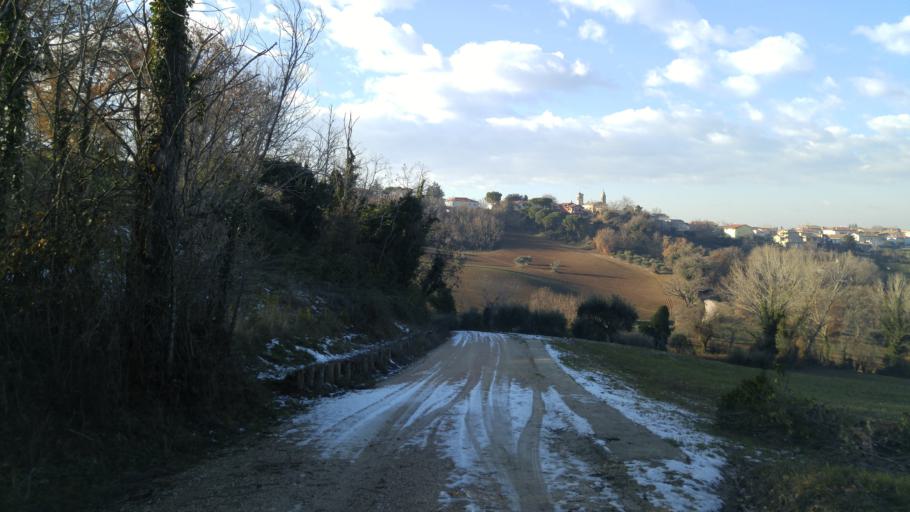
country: IT
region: The Marches
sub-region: Provincia di Pesaro e Urbino
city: Piagge
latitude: 43.7295
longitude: 12.9722
